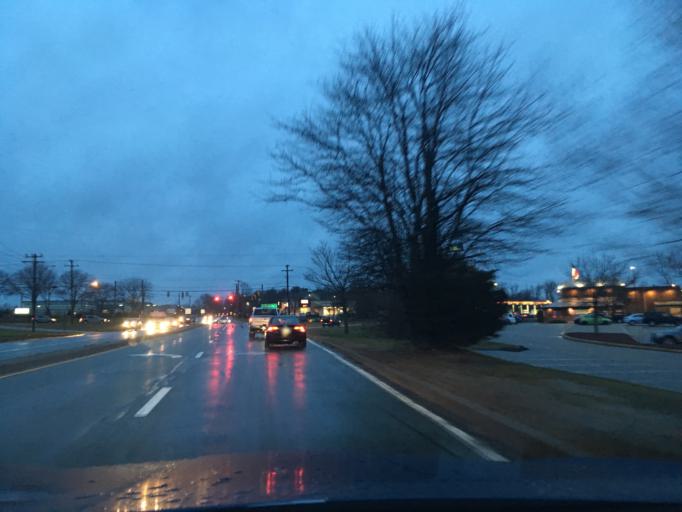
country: US
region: Rhode Island
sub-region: Kent County
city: East Greenwich
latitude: 41.6629
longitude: -71.4961
